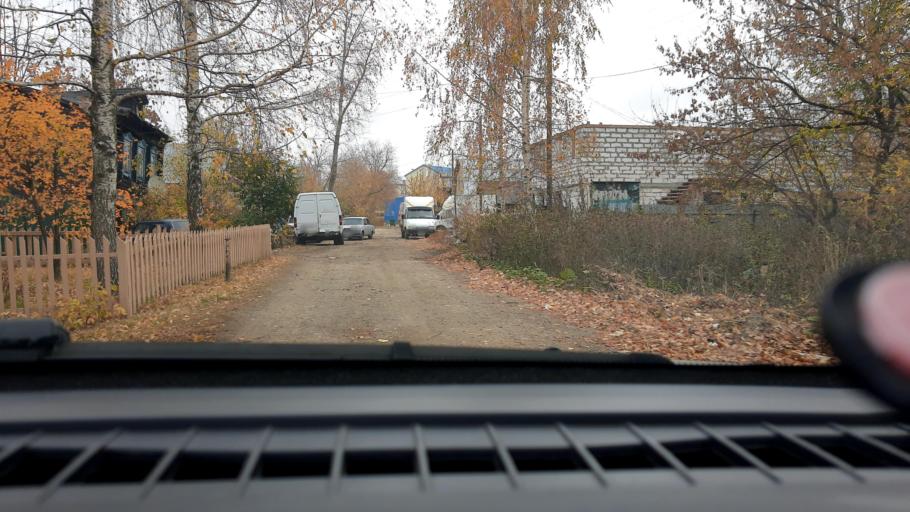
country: RU
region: Nizjnij Novgorod
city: Nizhniy Novgorod
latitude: 56.3159
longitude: 43.9339
